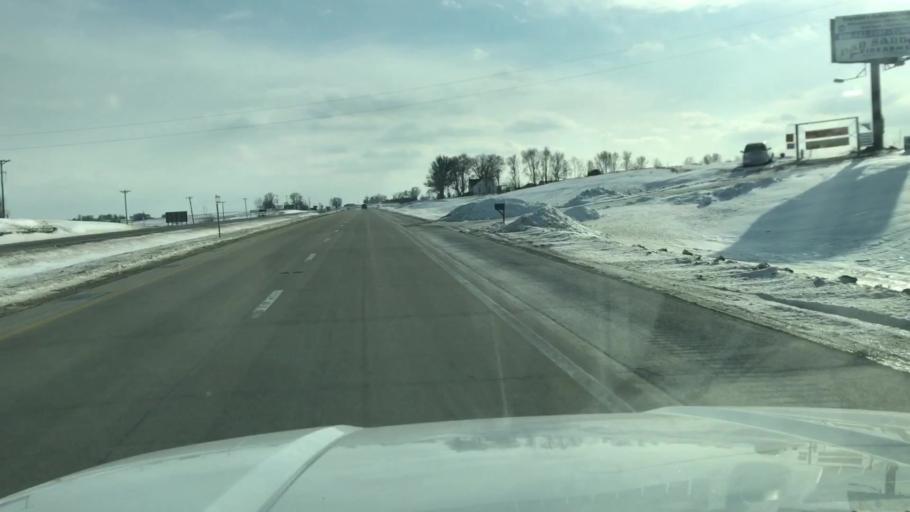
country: US
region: Missouri
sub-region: Nodaway County
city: Maryville
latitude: 40.2911
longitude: -94.8756
